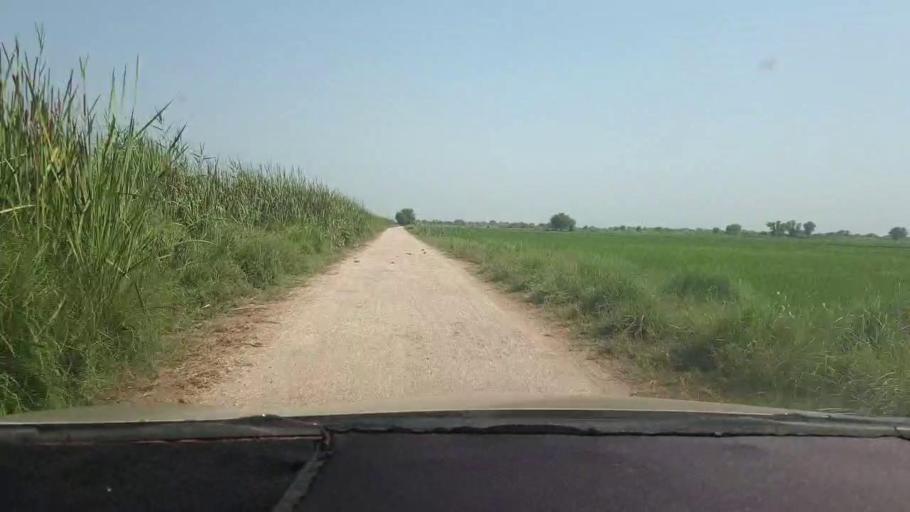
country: PK
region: Sindh
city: Miro Khan
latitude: 27.7000
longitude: 68.0918
